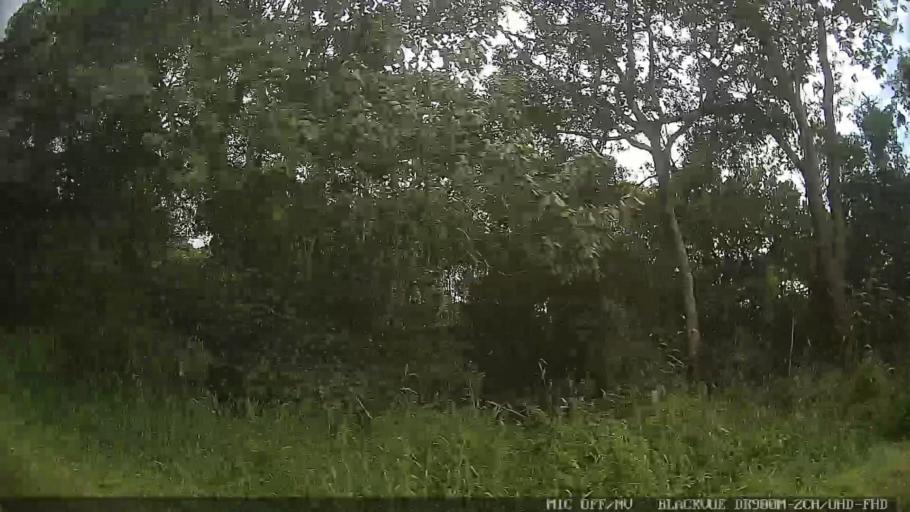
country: BR
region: Sao Paulo
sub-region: Ribeirao Pires
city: Ribeirao Pires
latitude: -23.6497
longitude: -46.3253
